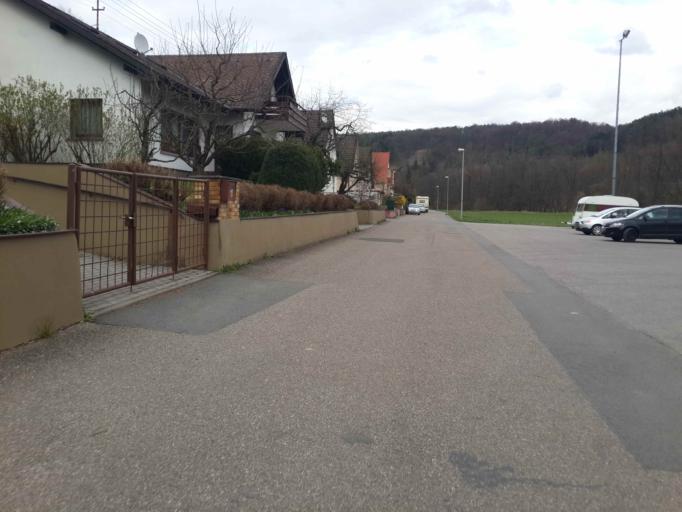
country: DE
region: Baden-Wuerttemberg
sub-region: Karlsruhe Region
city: Adelsheim
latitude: 49.3831
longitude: 9.3875
